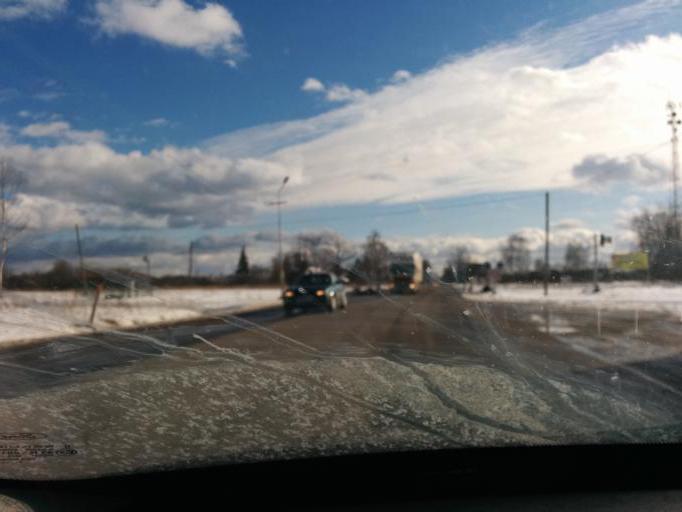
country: LV
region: Gulbenes Rajons
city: Gulbene
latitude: 57.1802
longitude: 26.7405
